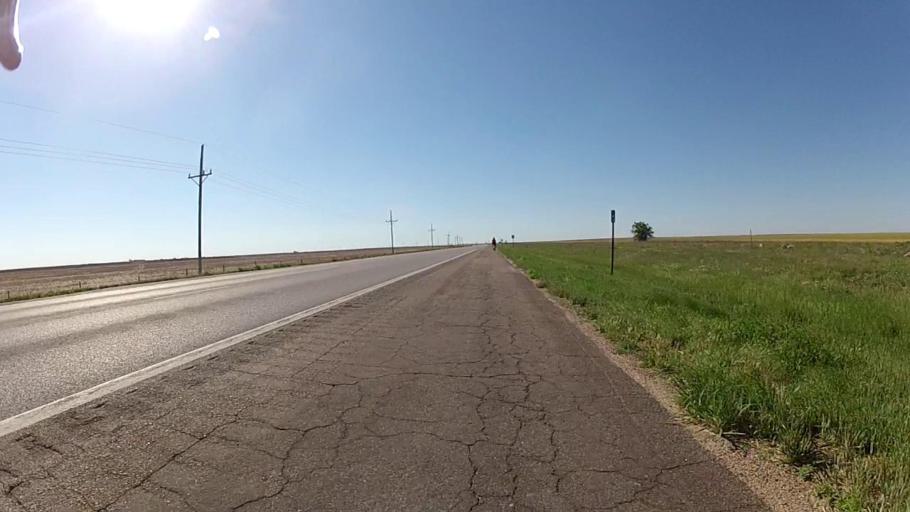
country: US
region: Kansas
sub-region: Ford County
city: Dodge City
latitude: 37.5914
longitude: -99.6896
